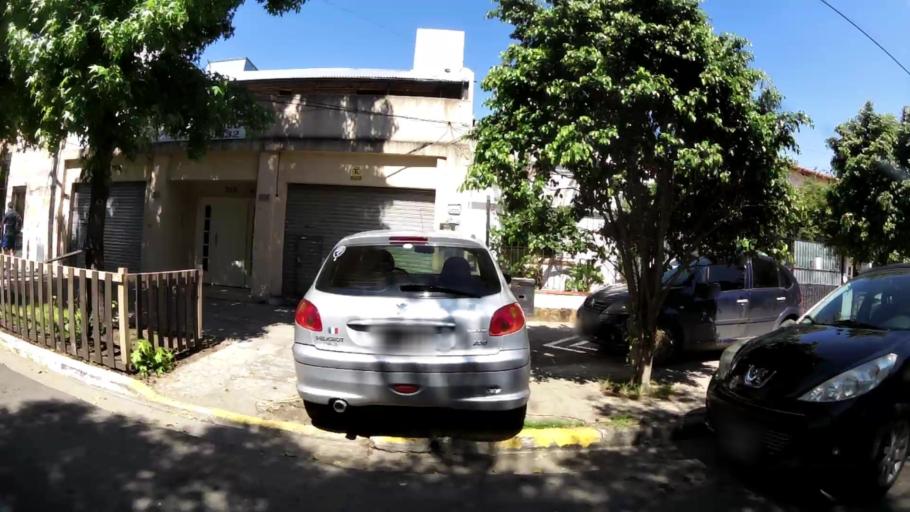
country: AR
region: Buenos Aires
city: Ituzaingo
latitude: -34.6560
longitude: -58.6658
